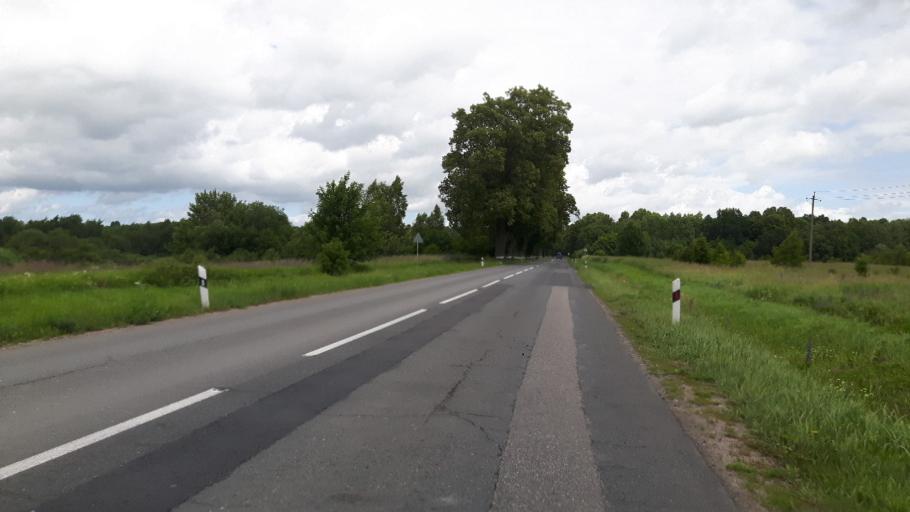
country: RU
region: Kaliningrad
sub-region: Gorod Kaliningrad
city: Kaliningrad
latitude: 54.8222
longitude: 20.4248
